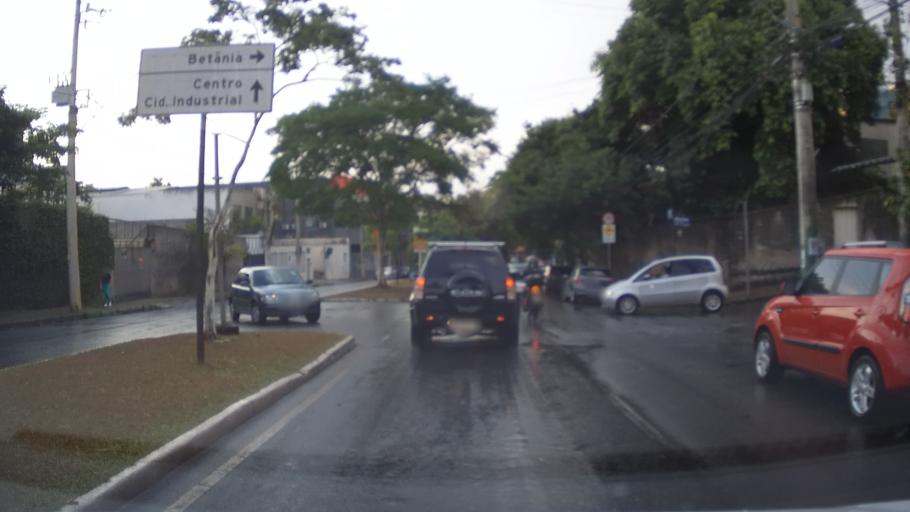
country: BR
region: Minas Gerais
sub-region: Belo Horizonte
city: Belo Horizonte
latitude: -19.9588
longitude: -43.9852
